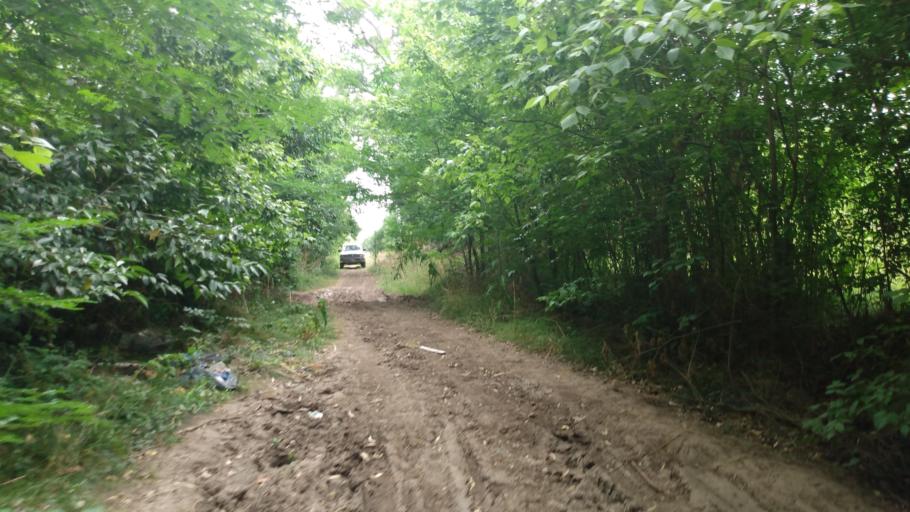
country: AR
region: Buenos Aires
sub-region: Partido de Lujan
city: Lujan
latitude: -34.5990
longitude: -59.0602
